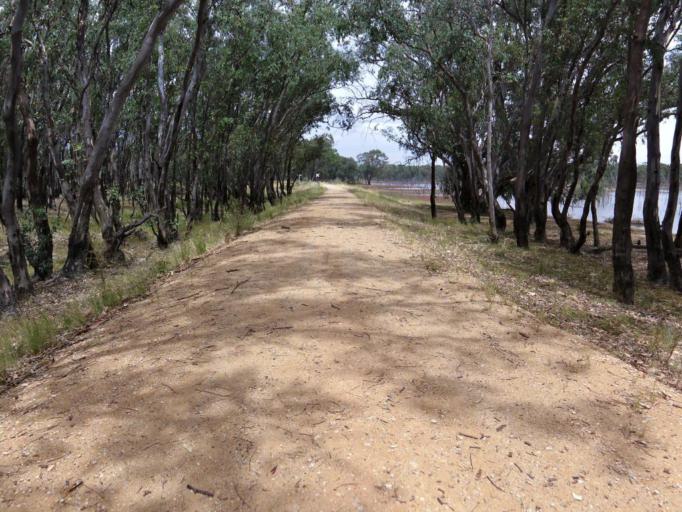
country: AU
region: Victoria
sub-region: Greater Bendigo
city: Kennington
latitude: -36.8701
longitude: 144.6256
